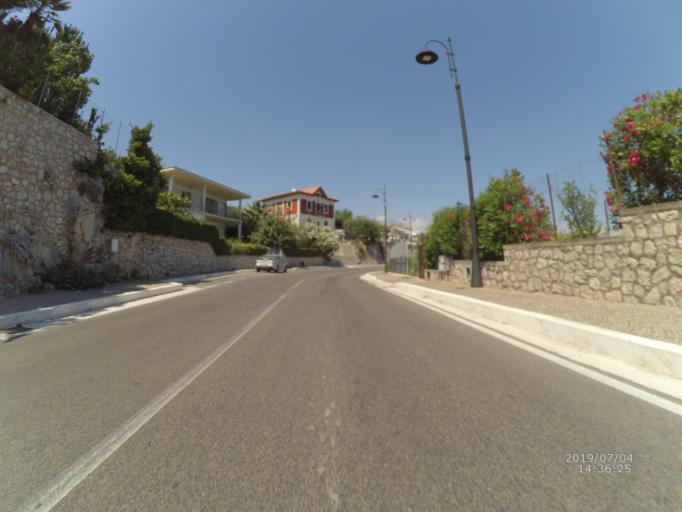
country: IT
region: Latium
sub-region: Provincia di Latina
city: Gaeta
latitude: 41.2100
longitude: 13.5540
